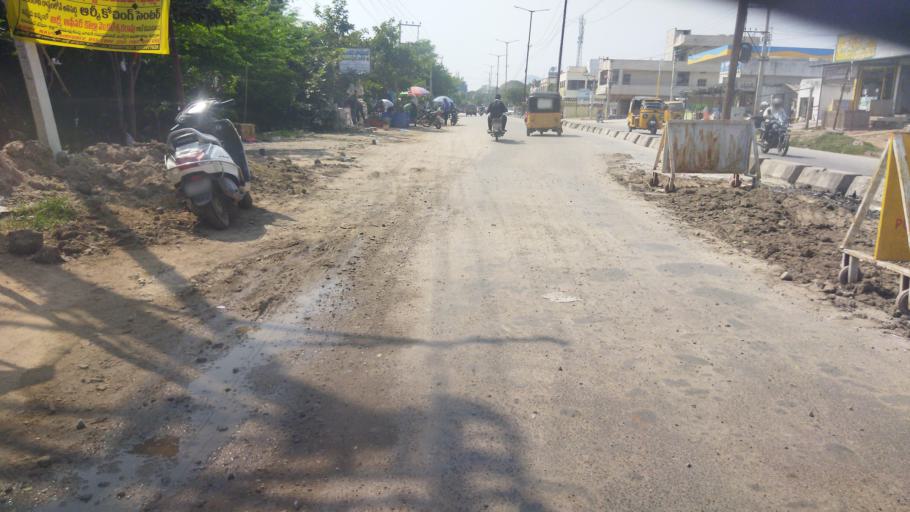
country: IN
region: Telangana
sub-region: Nalgonda
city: Nalgonda
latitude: 17.0730
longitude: 79.2852
